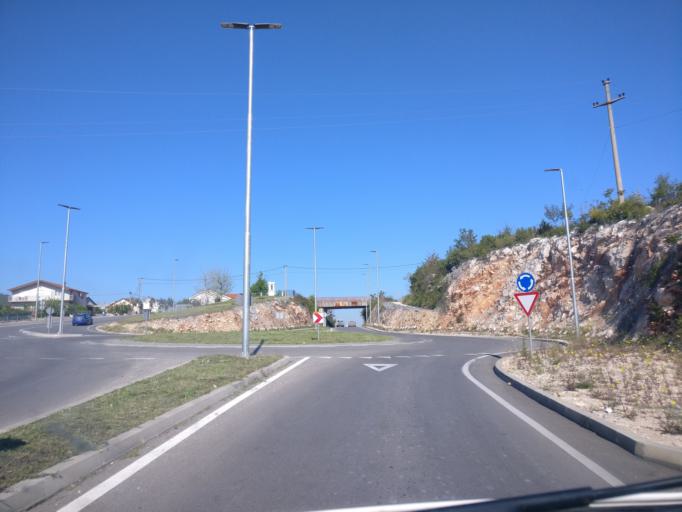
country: BA
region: Federation of Bosnia and Herzegovina
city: Capljina
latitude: 43.1417
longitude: 17.6634
